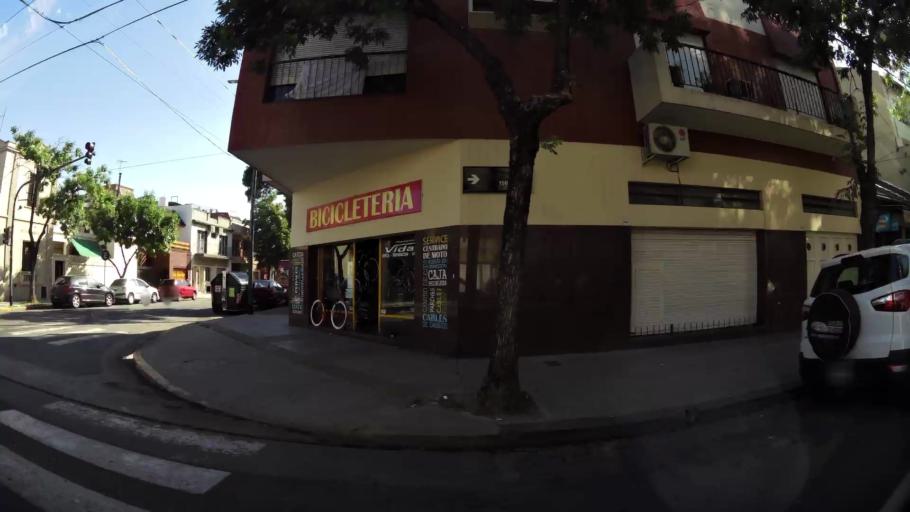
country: AR
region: Buenos Aires F.D.
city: Villa Santa Rita
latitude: -34.6122
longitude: -58.4672
